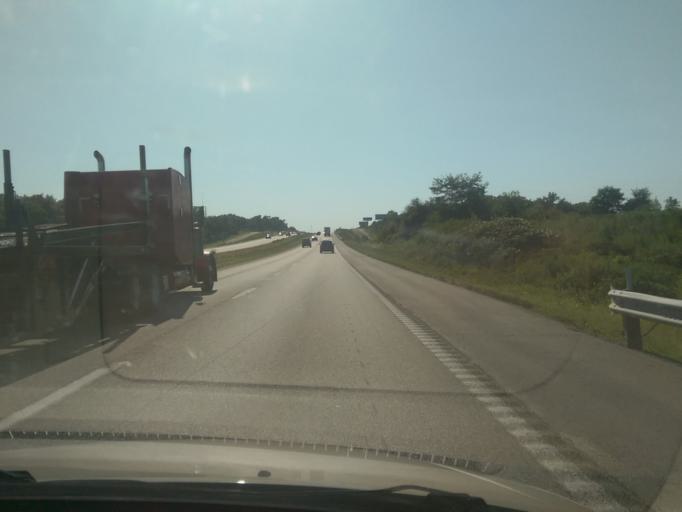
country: US
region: Missouri
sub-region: Saline County
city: Sweet Springs
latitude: 38.9747
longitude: -93.3630
